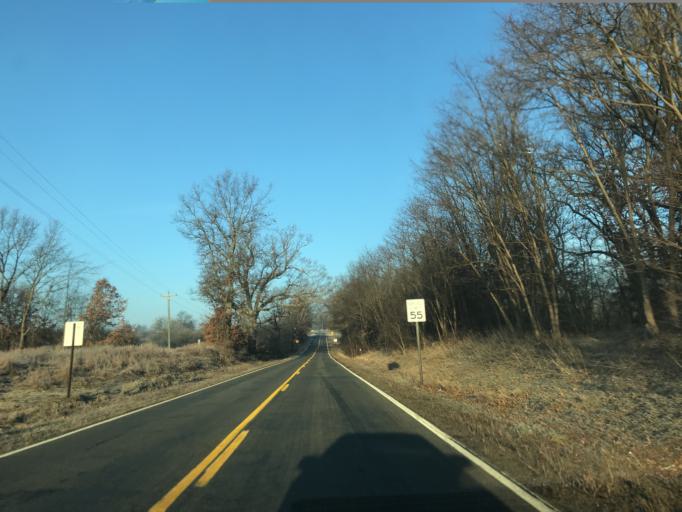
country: US
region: Michigan
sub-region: Eaton County
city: Eaton Rapids
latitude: 42.4483
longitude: -84.5689
